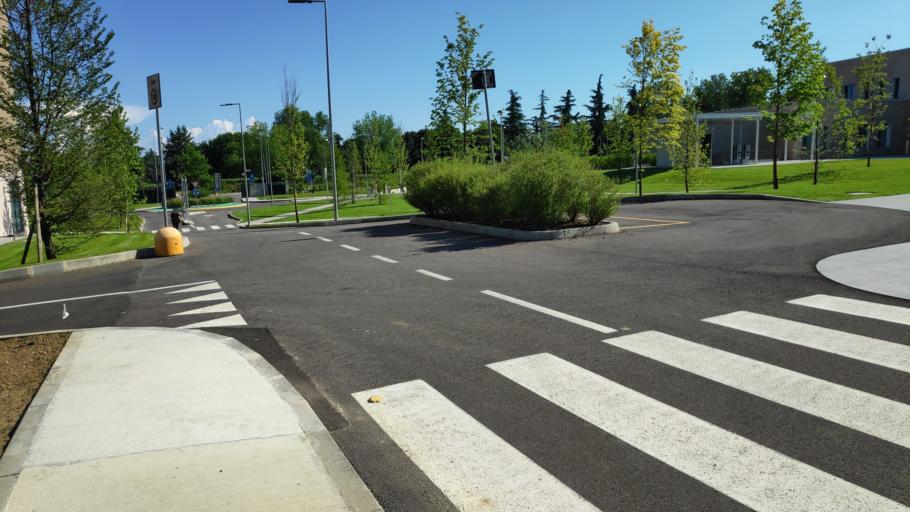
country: IT
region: Lombardy
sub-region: Citta metropolitana di Milano
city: Basiglio
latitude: 45.3700
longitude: 9.1723
